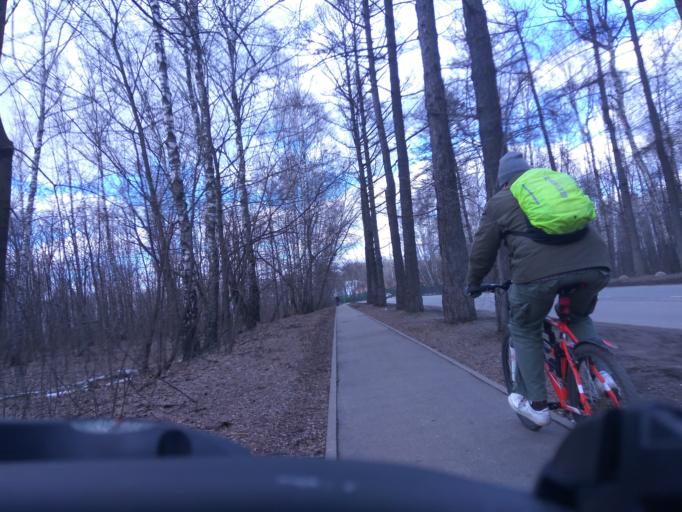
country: RU
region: Moscow
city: Sokol'niki
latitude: 55.8001
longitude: 37.6576
